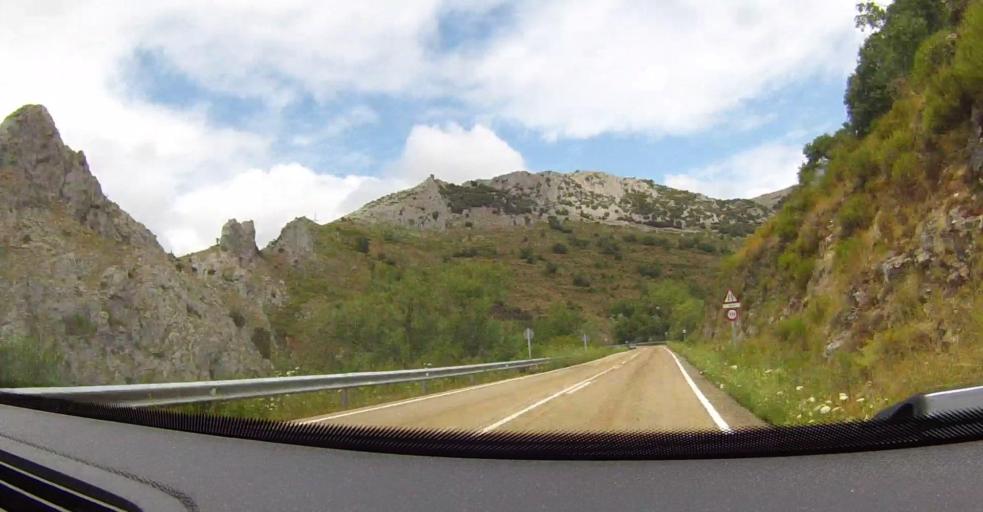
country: ES
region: Castille and Leon
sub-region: Provincia de Leon
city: Puebla de Lillo
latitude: 42.9589
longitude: -5.2512
